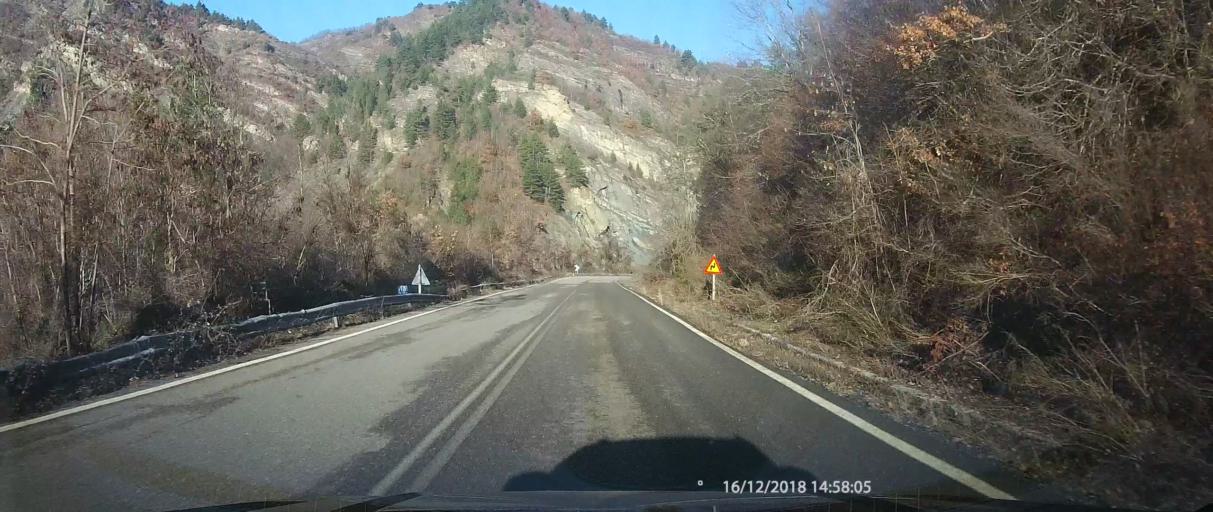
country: GR
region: West Macedonia
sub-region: Nomos Kastorias
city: Nestorio
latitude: 40.2211
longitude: 21.0289
